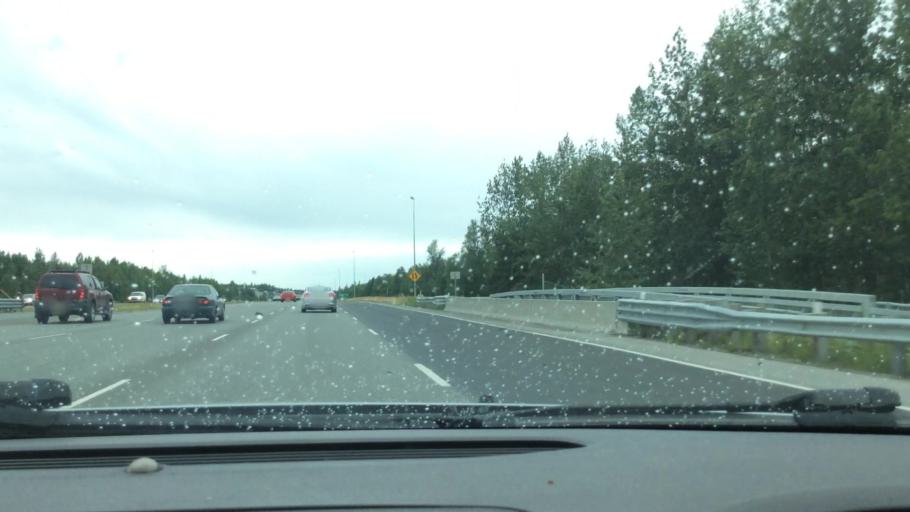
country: US
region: Alaska
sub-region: Anchorage Municipality
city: Elmendorf Air Force Base
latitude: 61.2385
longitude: -149.6939
